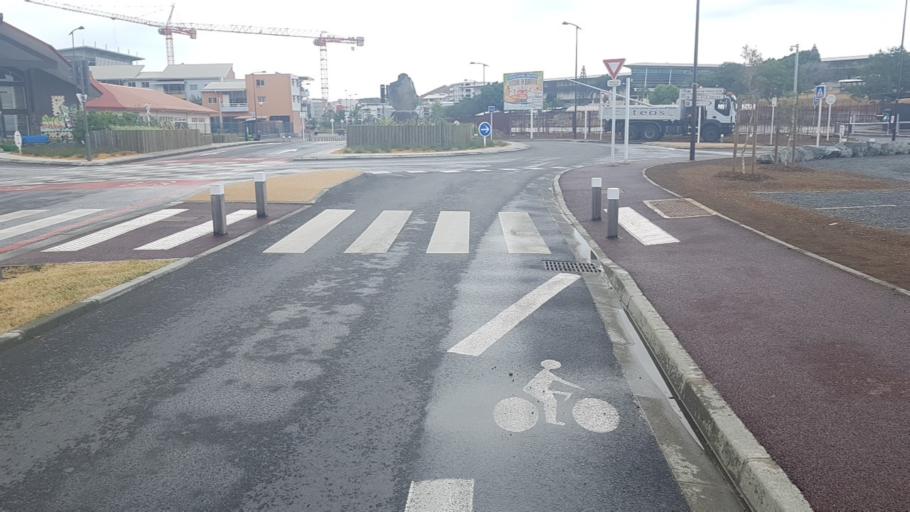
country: NC
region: South Province
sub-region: Noumea
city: Noumea
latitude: -22.2161
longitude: 166.4717
